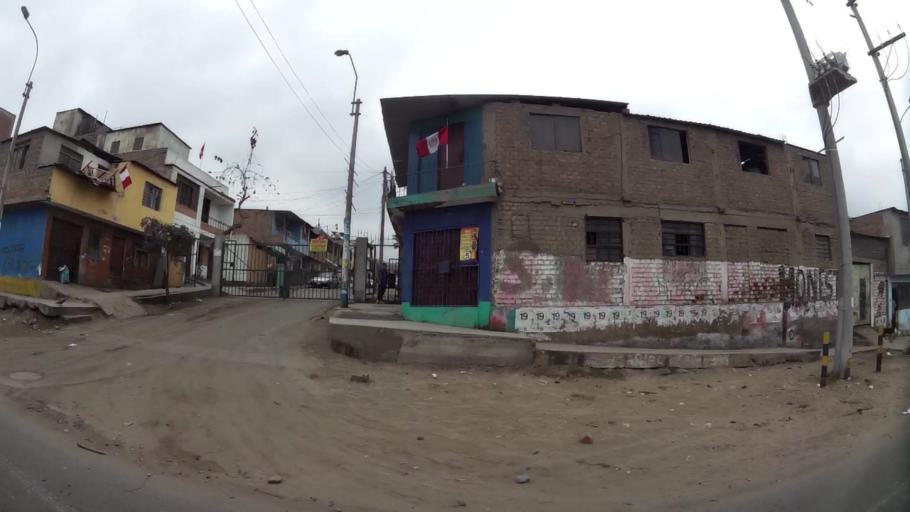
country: PE
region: Lima
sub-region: Lima
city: Surco
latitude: -12.1389
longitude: -76.9683
